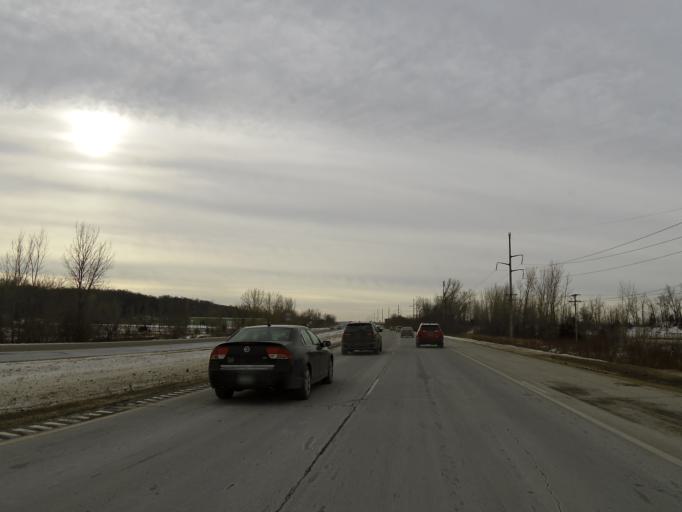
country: US
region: Minnesota
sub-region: Carver County
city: Chaska
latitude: 44.7544
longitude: -93.5856
